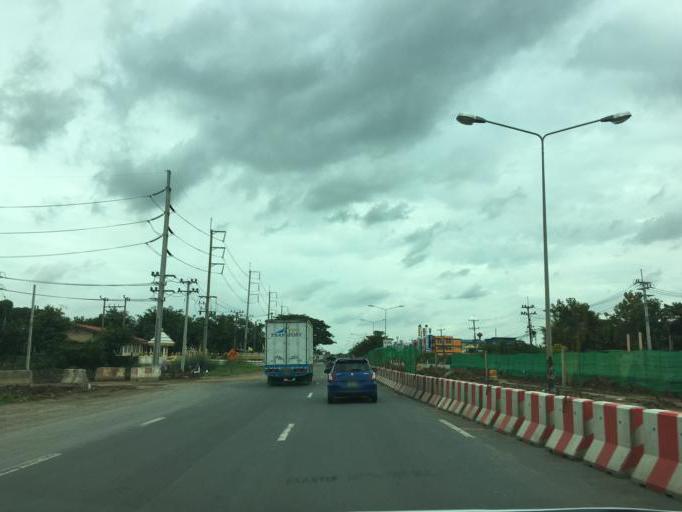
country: TH
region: Phra Nakhon Si Ayutthaya
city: Wang Noi
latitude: 14.2705
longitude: 100.6858
